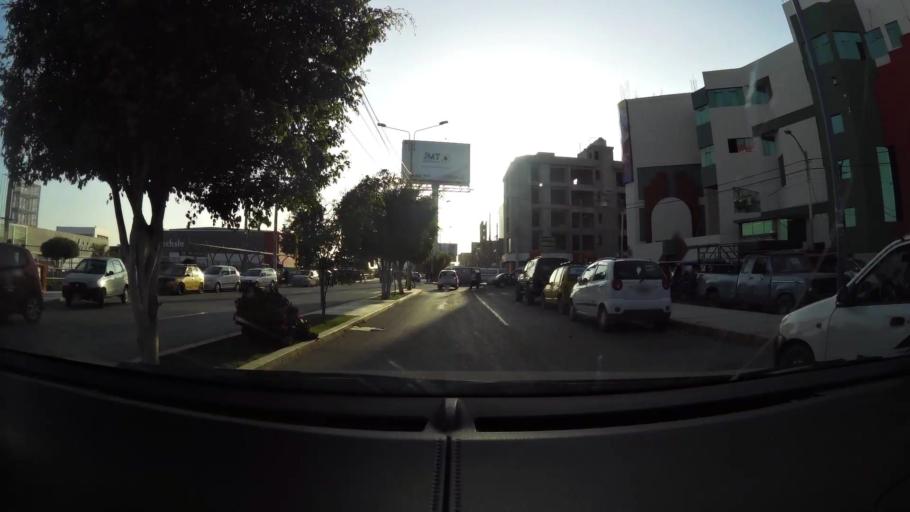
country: PE
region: Lambayeque
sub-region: Provincia de Chiclayo
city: Santa Rosa
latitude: -6.7765
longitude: -79.8319
